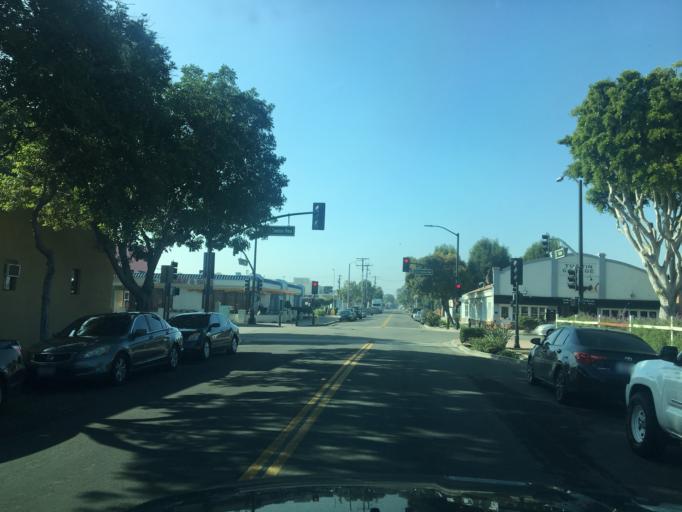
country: US
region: California
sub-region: Orange County
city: Tustin
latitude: 33.7401
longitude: -117.8232
